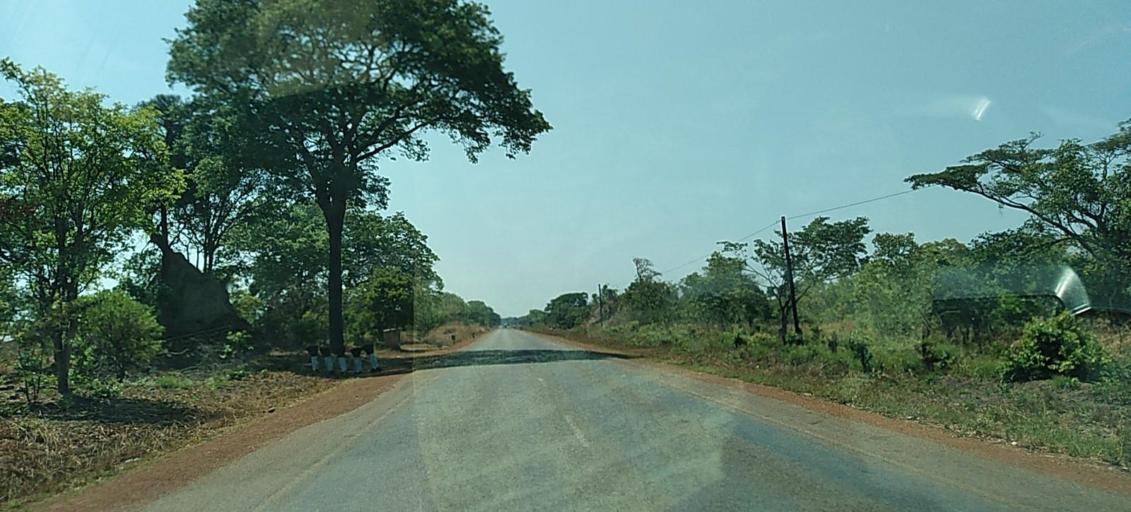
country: ZM
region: North-Western
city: Solwezi
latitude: -12.3530
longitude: 25.9235
